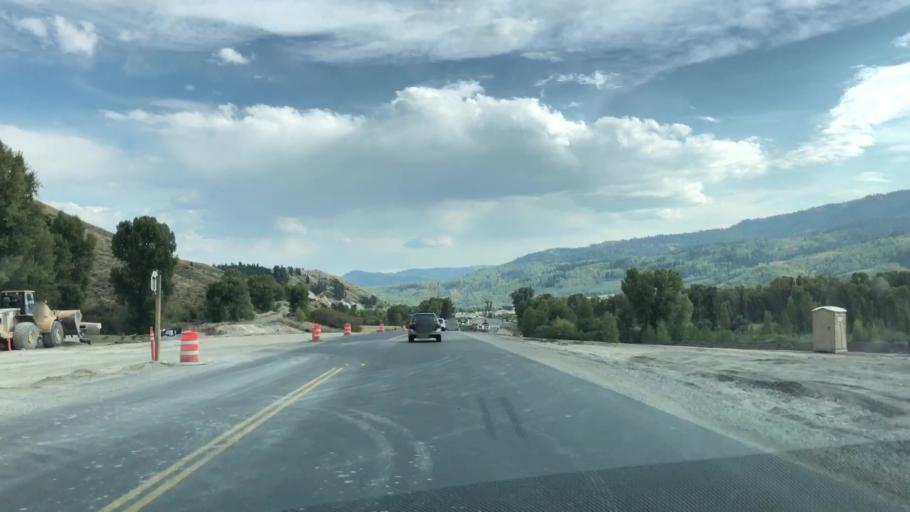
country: US
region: Wyoming
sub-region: Teton County
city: South Park
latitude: 43.3941
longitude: -110.7482
